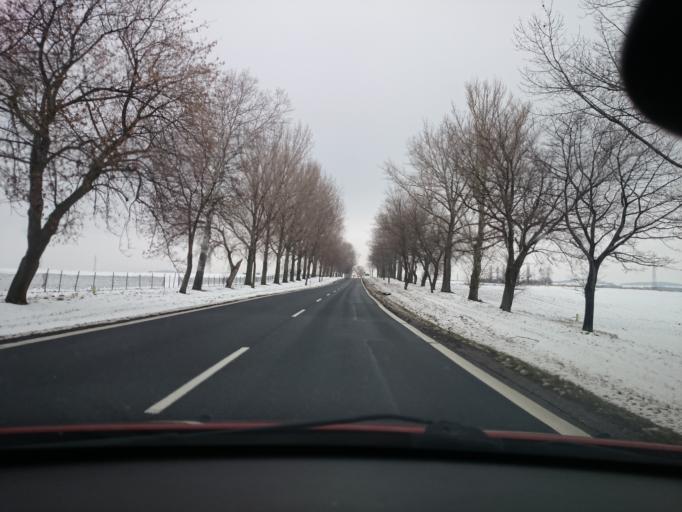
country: PL
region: Lower Silesian Voivodeship
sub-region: Powiat zabkowicki
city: Zabkowice Slaskie
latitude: 50.5759
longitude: 16.7968
